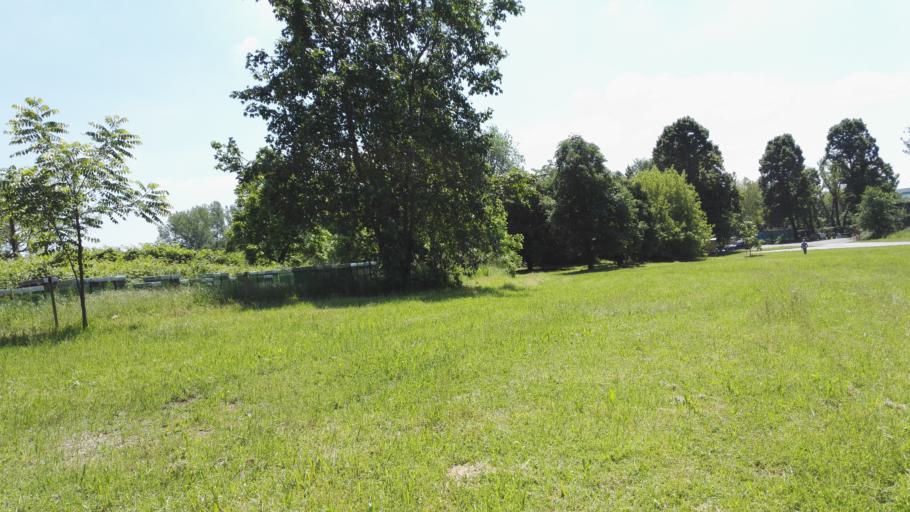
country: IT
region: Lombardy
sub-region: Citta metropolitana di Milano
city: San Donato Milanese
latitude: 45.4196
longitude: 9.2889
